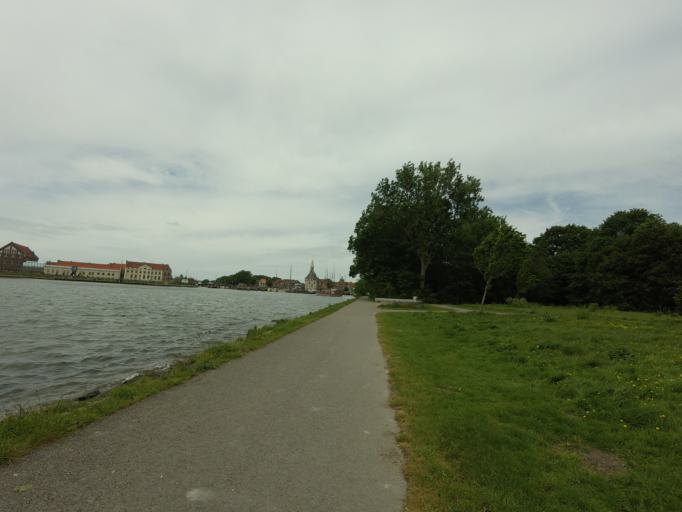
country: NL
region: North Holland
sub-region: Gemeente Hoorn
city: Hoorn
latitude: 52.6357
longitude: 5.0668
